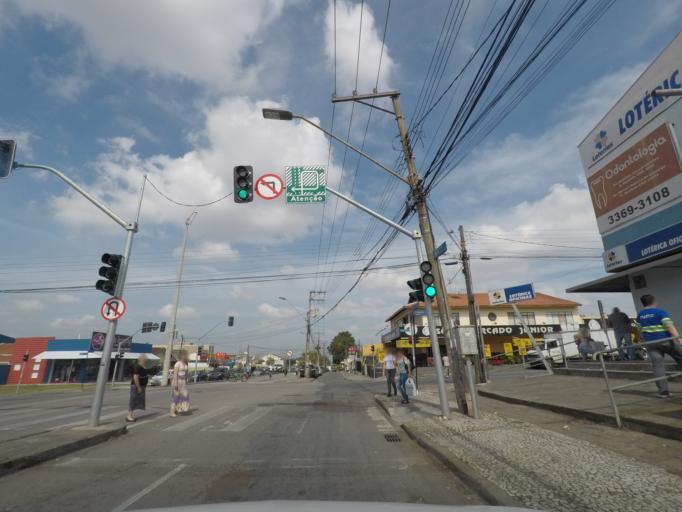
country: BR
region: Parana
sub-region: Pinhais
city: Pinhais
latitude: -25.4541
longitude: -49.2143
